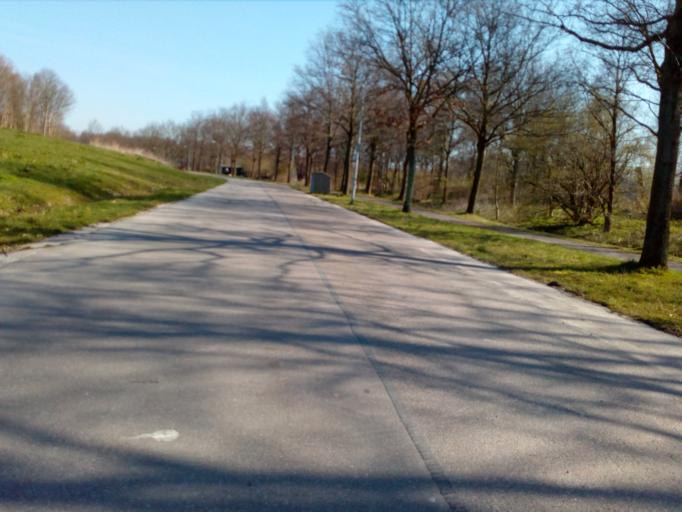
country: NL
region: South Holland
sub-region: Gemeente Rijswijk
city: Rijswijk
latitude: 52.0261
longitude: 4.3293
